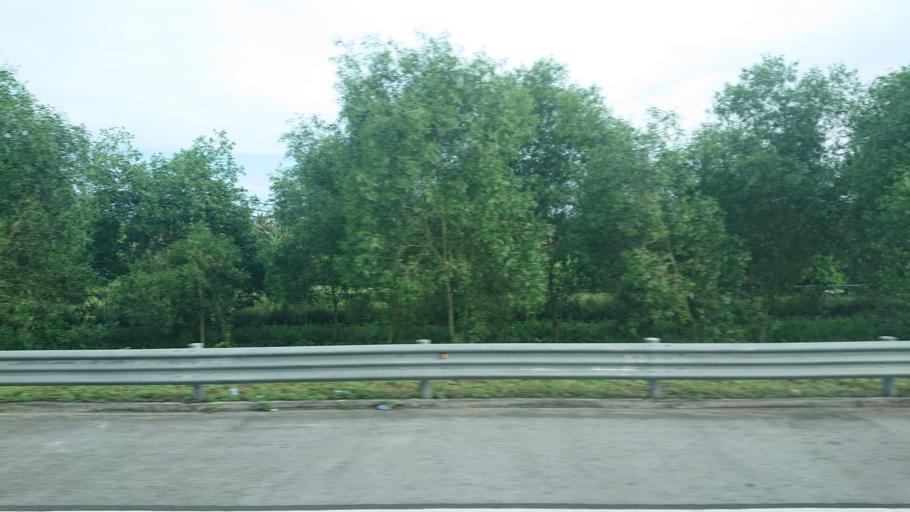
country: VN
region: Hai Phong
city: Nui Doi
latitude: 20.7655
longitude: 106.6626
